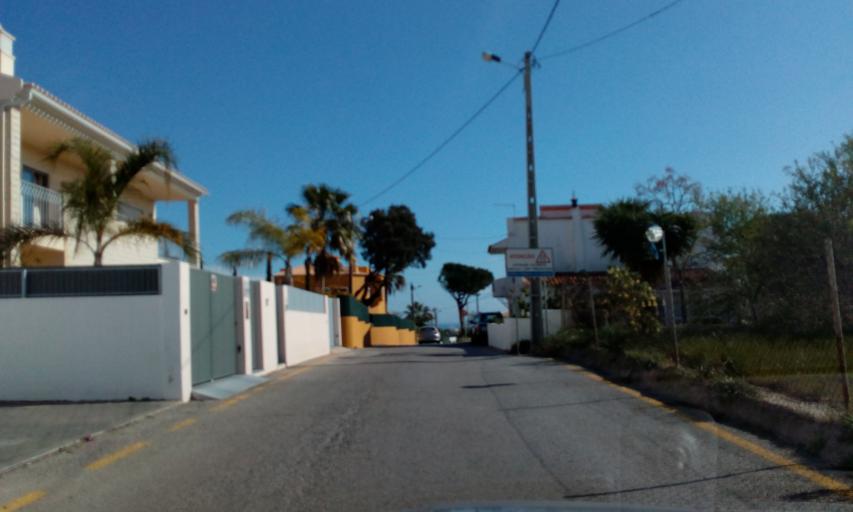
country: PT
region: Faro
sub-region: Albufeira
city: Ferreiras
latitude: 37.1073
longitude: -8.2116
